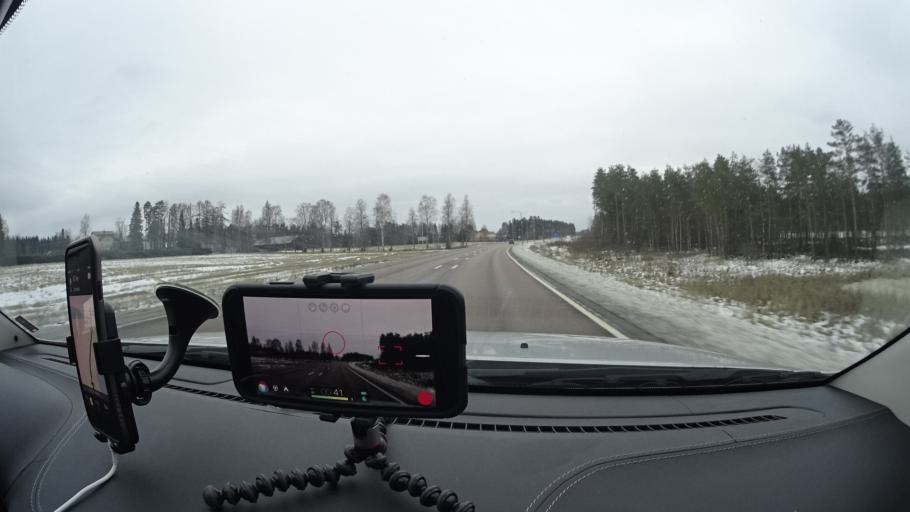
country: FI
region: Paijanne Tavastia
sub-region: Lahti
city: Hartola
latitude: 61.4997
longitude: 25.9799
